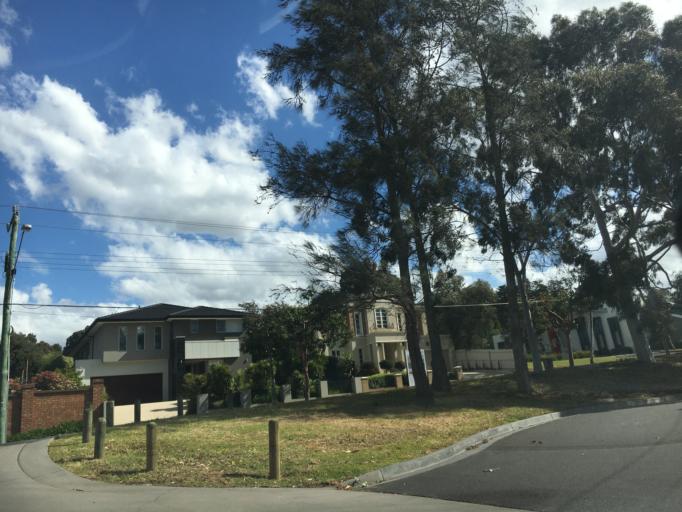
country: AU
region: Victoria
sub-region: Monash
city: Mulgrave
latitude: -37.8908
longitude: 145.1840
